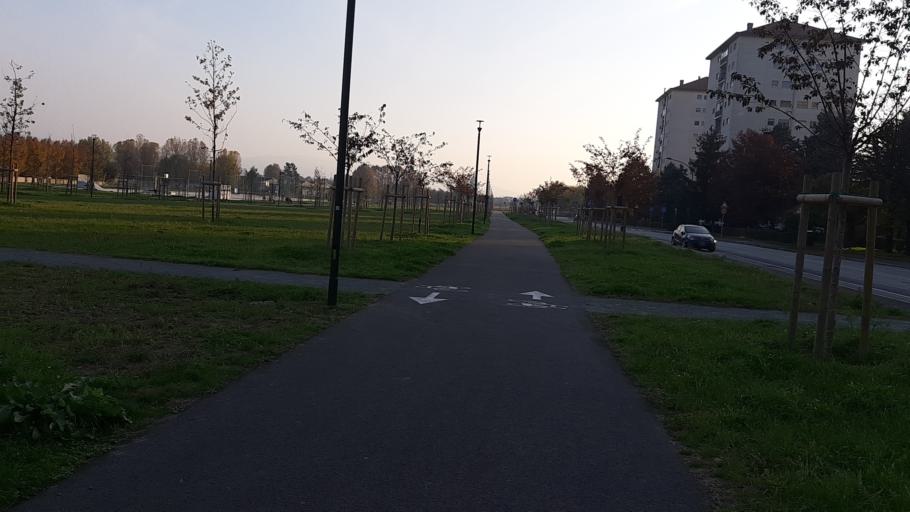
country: IT
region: Piedmont
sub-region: Provincia di Torino
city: Settimo Torinese
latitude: 45.1293
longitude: 7.7164
